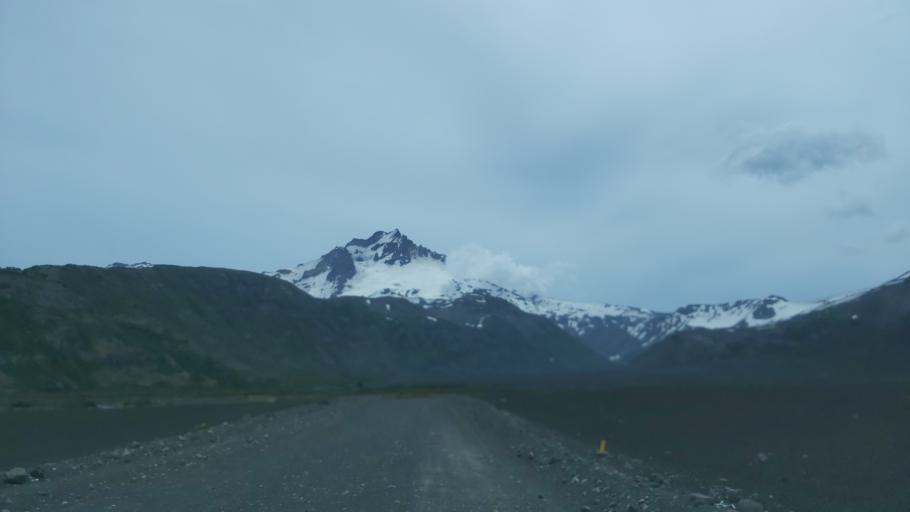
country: AR
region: Neuquen
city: Andacollo
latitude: -37.4612
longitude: -71.3105
